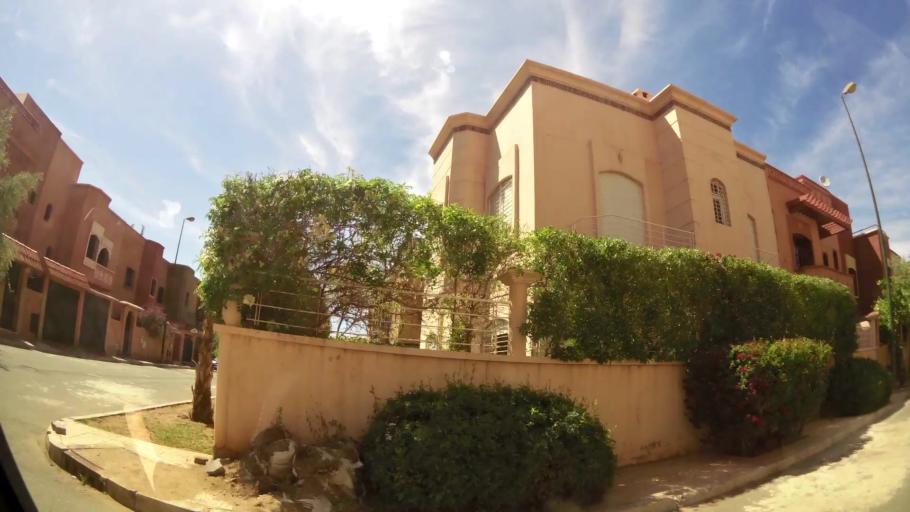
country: MA
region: Marrakech-Tensift-Al Haouz
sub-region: Marrakech
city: Marrakesh
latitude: 31.6606
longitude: -7.9907
